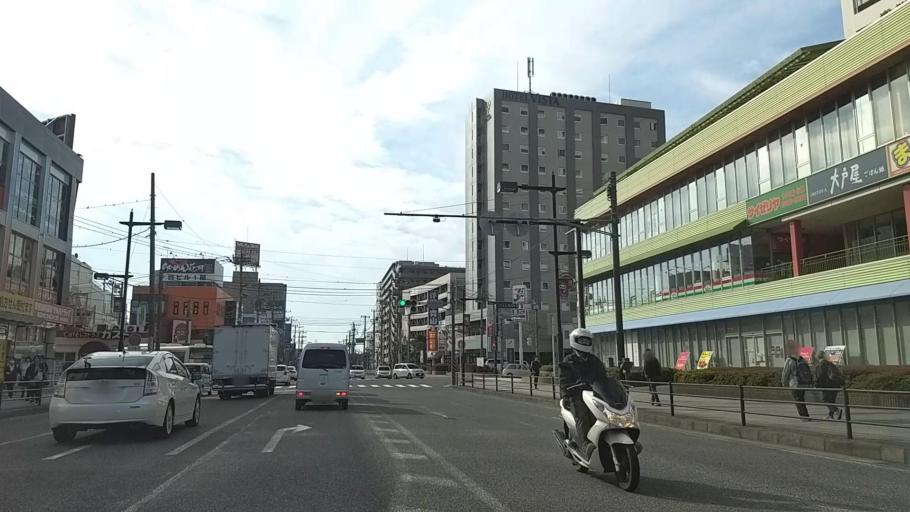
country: JP
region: Kanagawa
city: Atsugi
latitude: 35.4518
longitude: 139.3923
